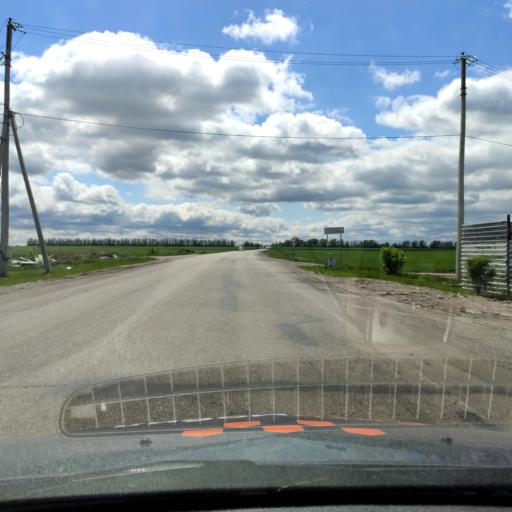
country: RU
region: Voronezj
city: Novaya Usman'
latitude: 51.5989
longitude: 39.3387
